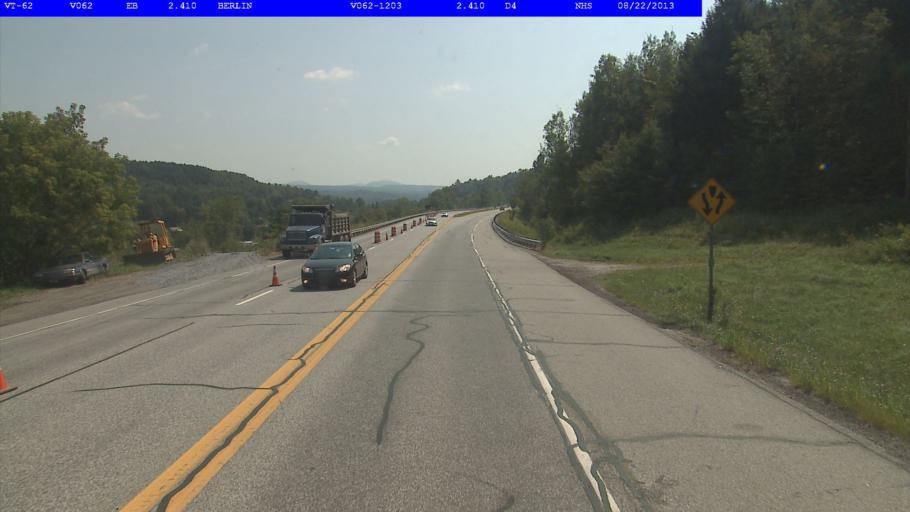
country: US
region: Vermont
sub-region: Washington County
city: Barre
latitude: 44.2167
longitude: -72.5428
